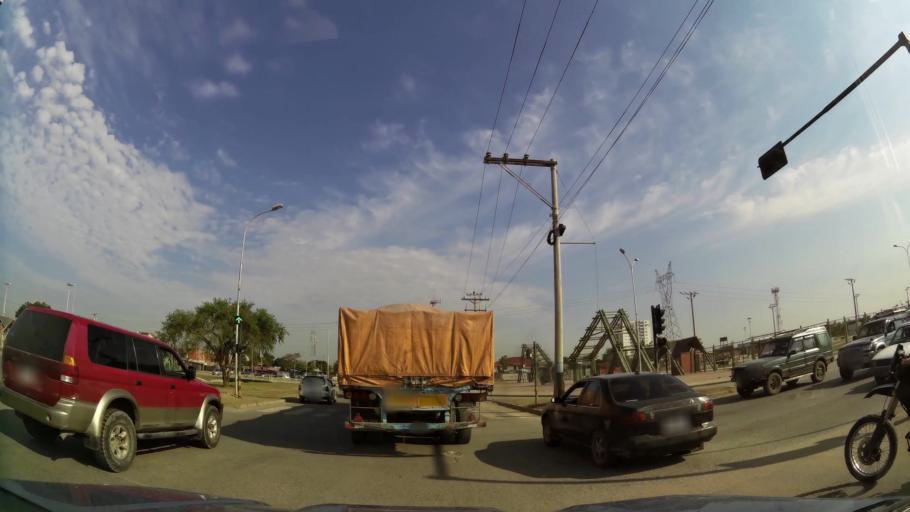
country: BO
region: Santa Cruz
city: Santa Cruz de la Sierra
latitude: -17.7426
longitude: -63.1449
